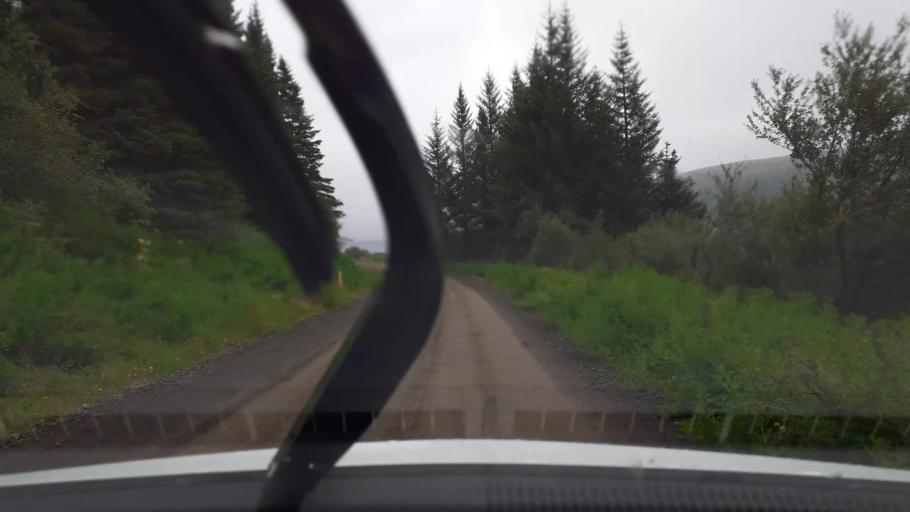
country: IS
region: Capital Region
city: Mosfellsbaer
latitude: 64.5157
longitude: -21.4145
